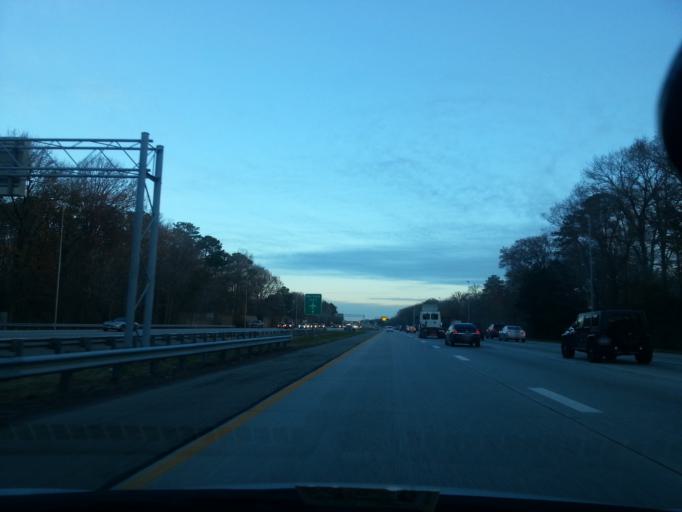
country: US
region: Virginia
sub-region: City of Chesapeake
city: Chesapeake
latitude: 36.8175
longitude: -76.1948
